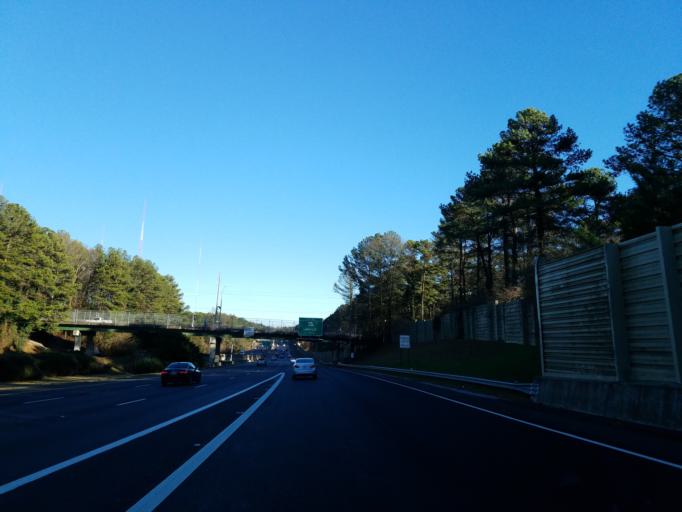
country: US
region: Georgia
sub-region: Fulton County
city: East Point
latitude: 33.7599
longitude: -84.4841
